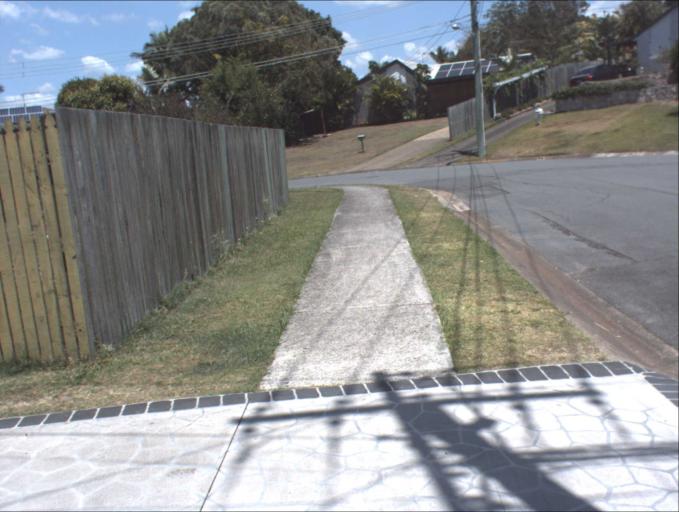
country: AU
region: Queensland
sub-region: Logan
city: Springwood
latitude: -27.5993
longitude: 153.1395
